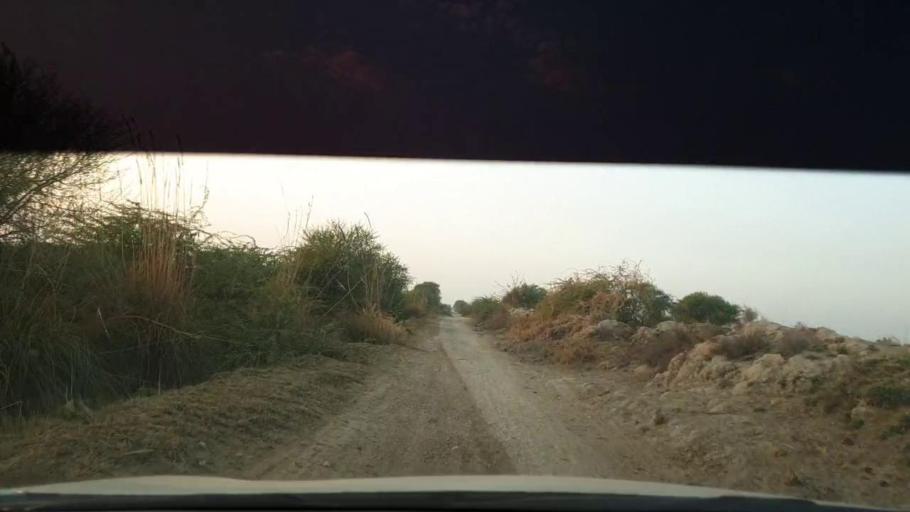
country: PK
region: Sindh
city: Berani
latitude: 25.7674
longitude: 68.9827
